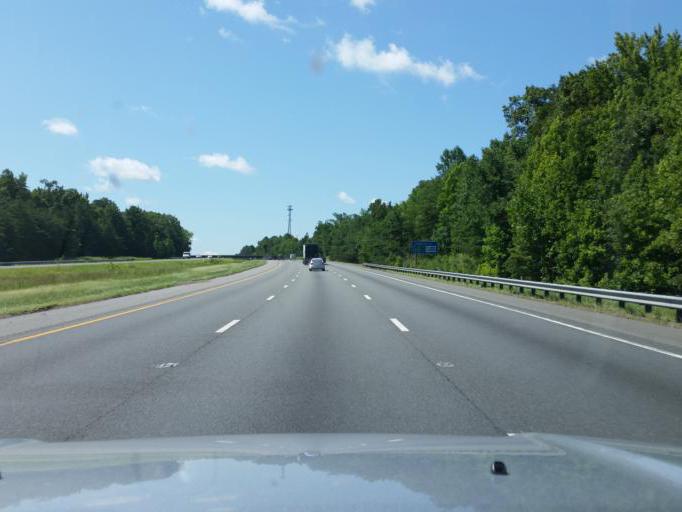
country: US
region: Virginia
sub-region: Spotsylvania County
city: Spotsylvania Courthouse
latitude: 38.1609
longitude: -77.5076
